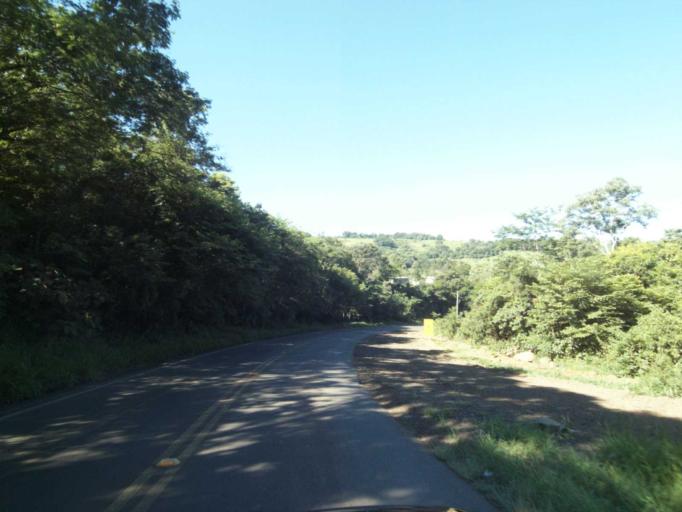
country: BR
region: Parana
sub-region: Francisco Beltrao
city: Francisco Beltrao
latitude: -26.1441
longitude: -53.3040
